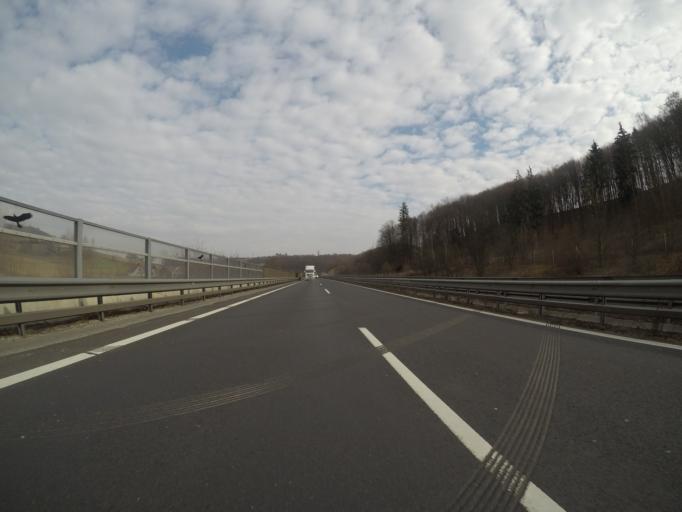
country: SI
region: Cerkvenjak
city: Cerkvenjak
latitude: 46.5807
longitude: 15.9572
